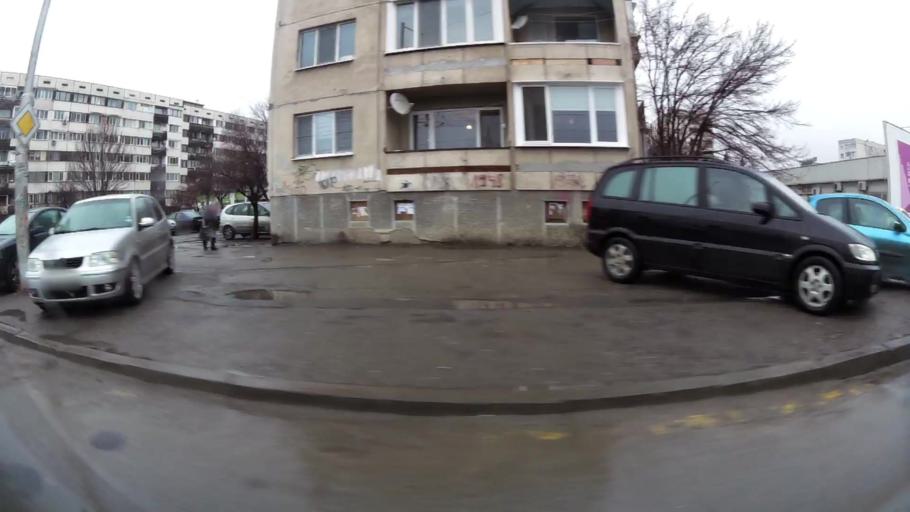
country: BG
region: Sofia-Capital
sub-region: Stolichna Obshtina
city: Sofia
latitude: 42.6571
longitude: 23.3999
